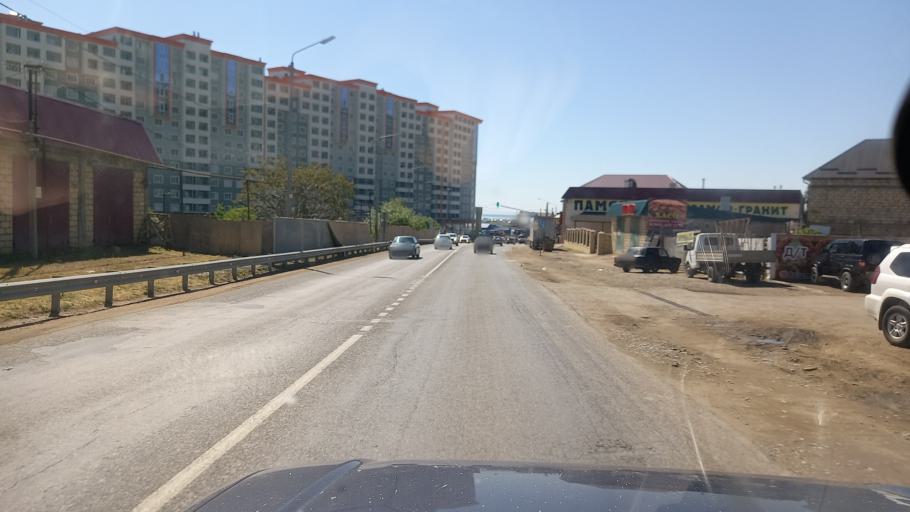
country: RU
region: Dagestan
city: Derbent
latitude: 42.0368
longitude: 48.2929
